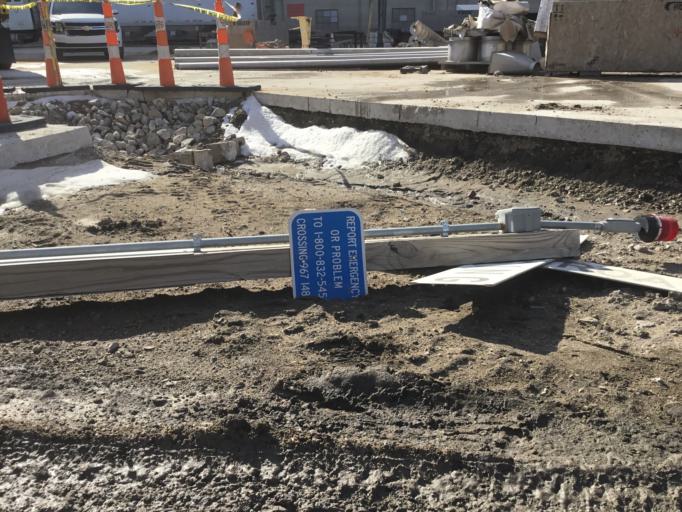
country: US
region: Kansas
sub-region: Sedgwick County
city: Wichita
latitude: 37.7056
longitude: -97.3290
